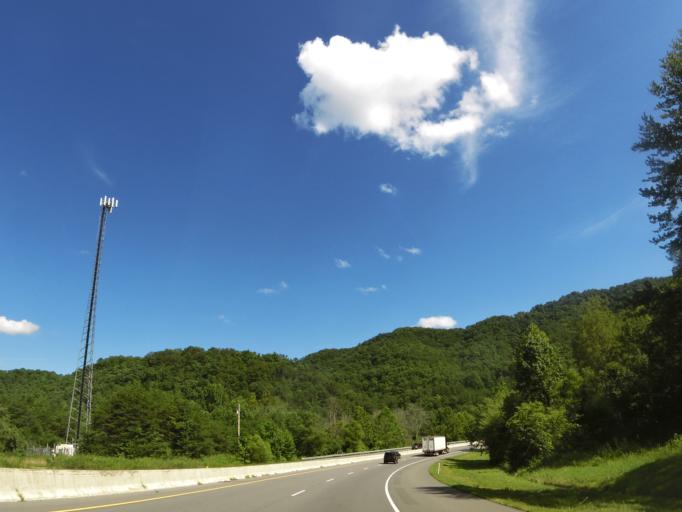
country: US
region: Tennessee
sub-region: Grainger County
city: Bean Station
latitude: 36.3605
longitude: -83.3382
